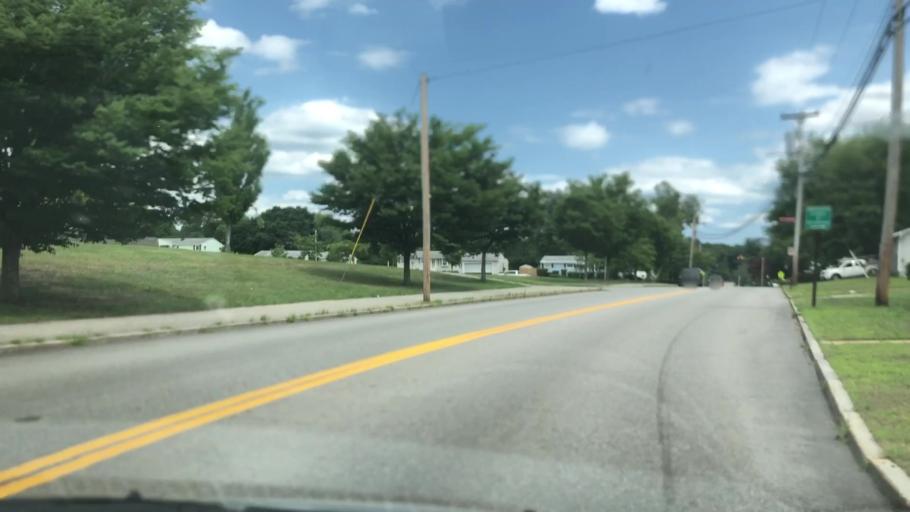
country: US
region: New Hampshire
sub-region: Hillsborough County
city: Manchester
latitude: 42.9648
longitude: -71.4351
